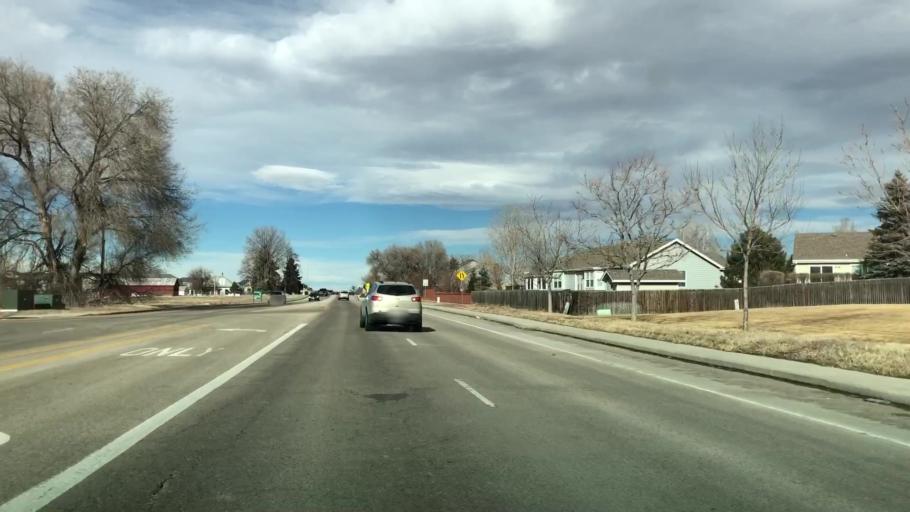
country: US
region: Colorado
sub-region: Weld County
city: Windsor
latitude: 40.4817
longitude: -104.9264
